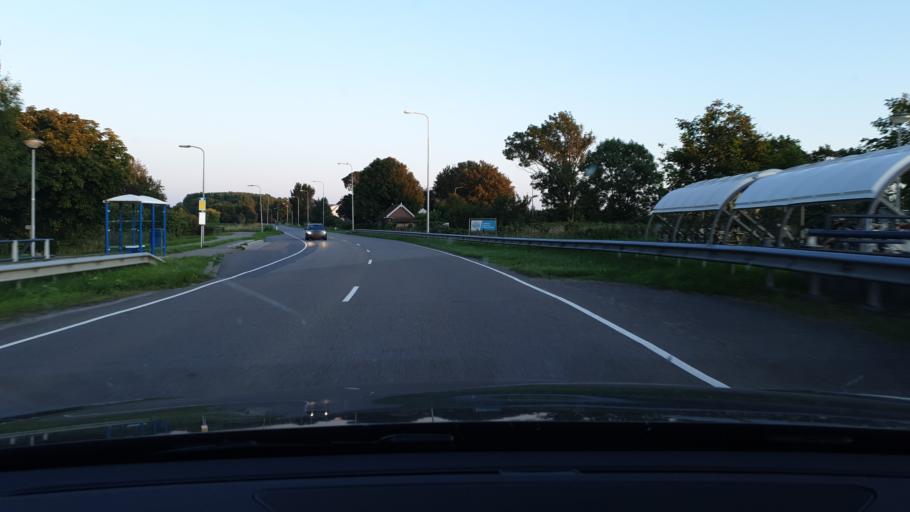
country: NL
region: South Holland
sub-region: Gemeente Goeree-Overflakkee
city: Dirksland
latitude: 51.7734
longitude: 4.0748
